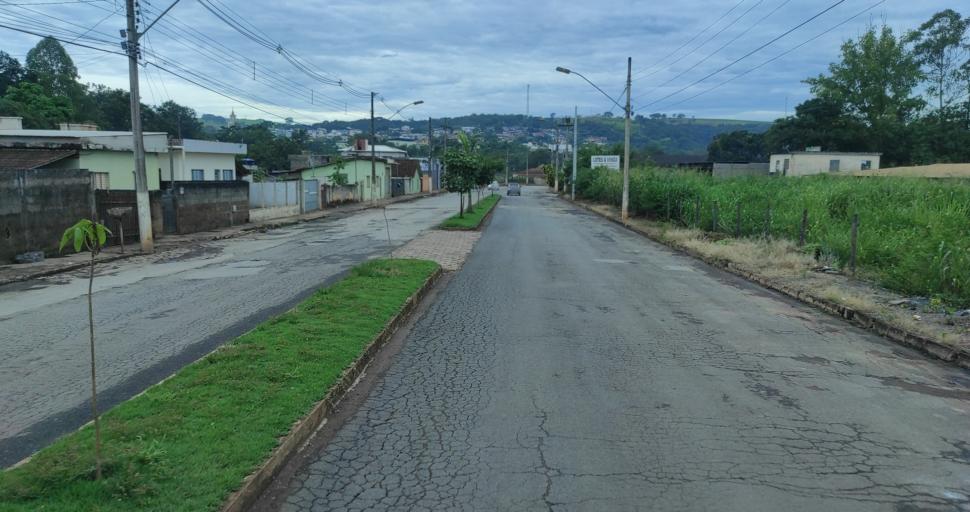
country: BR
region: Minas Gerais
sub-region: Arcos
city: Arcos
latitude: -20.3761
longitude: -45.6665
